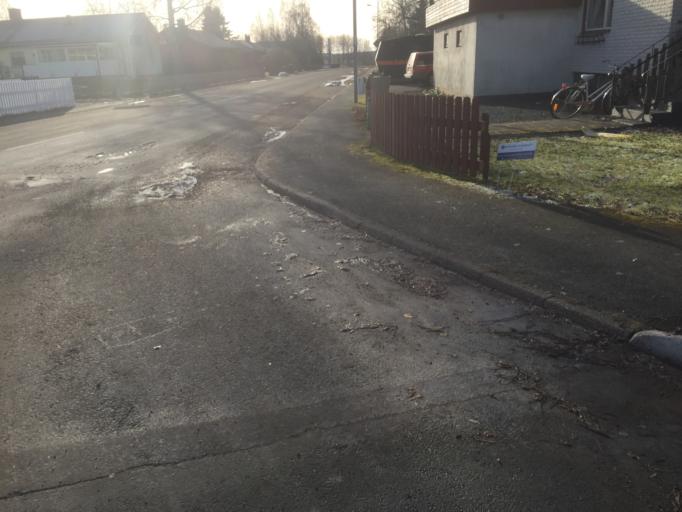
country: SE
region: Joenkoeping
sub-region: Aneby Kommun
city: Aneby
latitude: 57.8394
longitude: 14.8038
